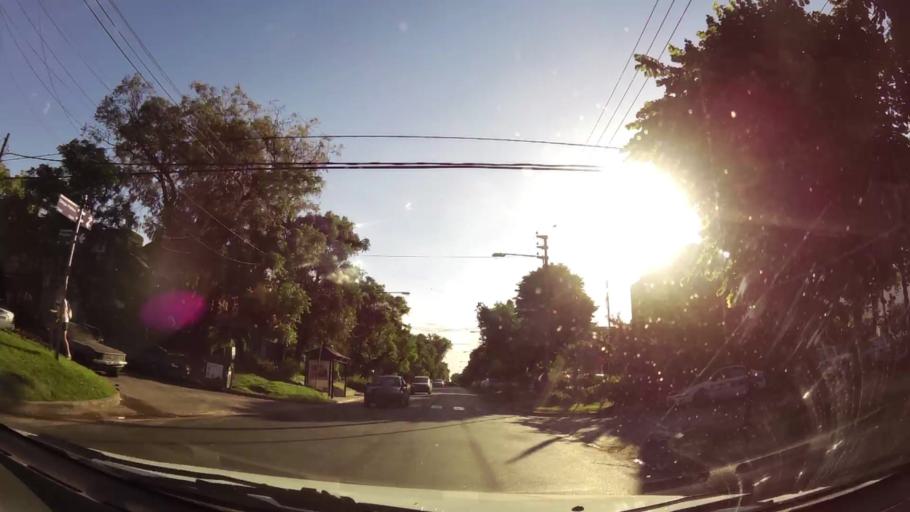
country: AR
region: Buenos Aires
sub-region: Partido de San Isidro
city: San Isidro
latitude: -34.4797
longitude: -58.5341
